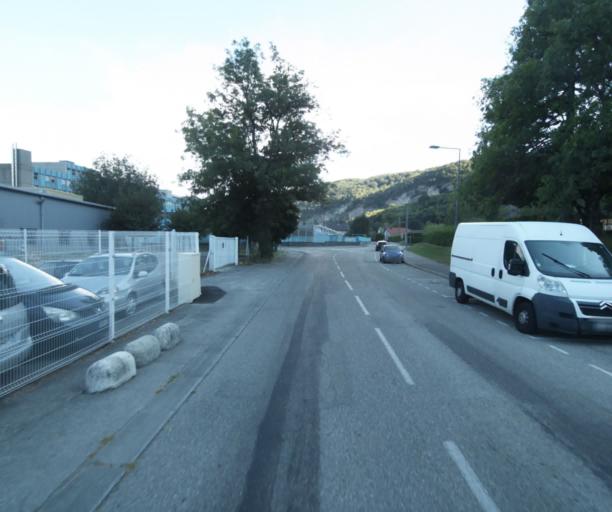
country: FR
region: Rhone-Alpes
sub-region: Departement de l'Isere
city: Sassenage
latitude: 45.1996
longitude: 5.6651
